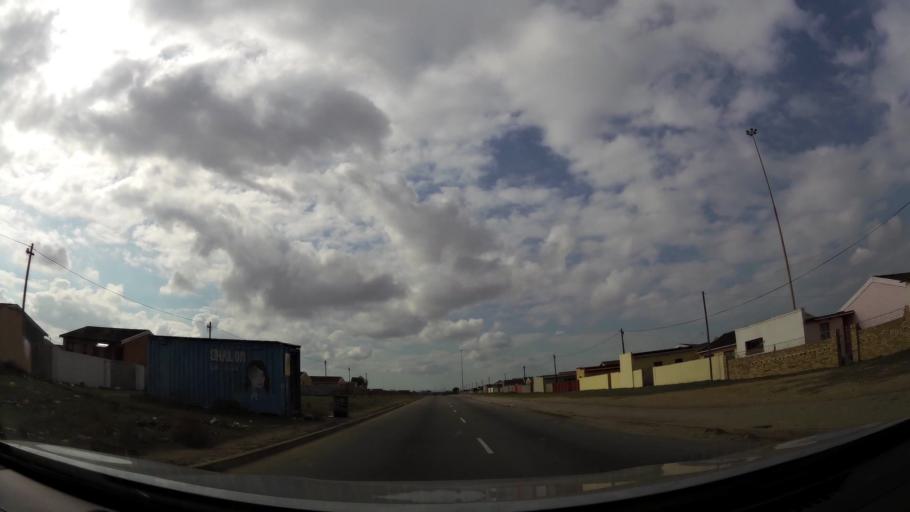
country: ZA
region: Eastern Cape
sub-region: Nelson Mandela Bay Metropolitan Municipality
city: Port Elizabeth
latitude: -33.8203
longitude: 25.5927
